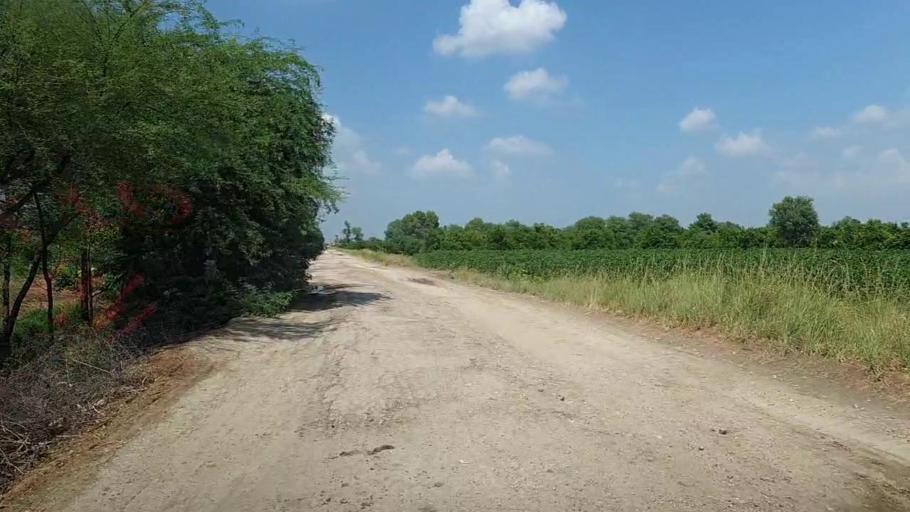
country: PK
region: Sindh
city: Kandiaro
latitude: 27.0232
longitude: 68.2727
